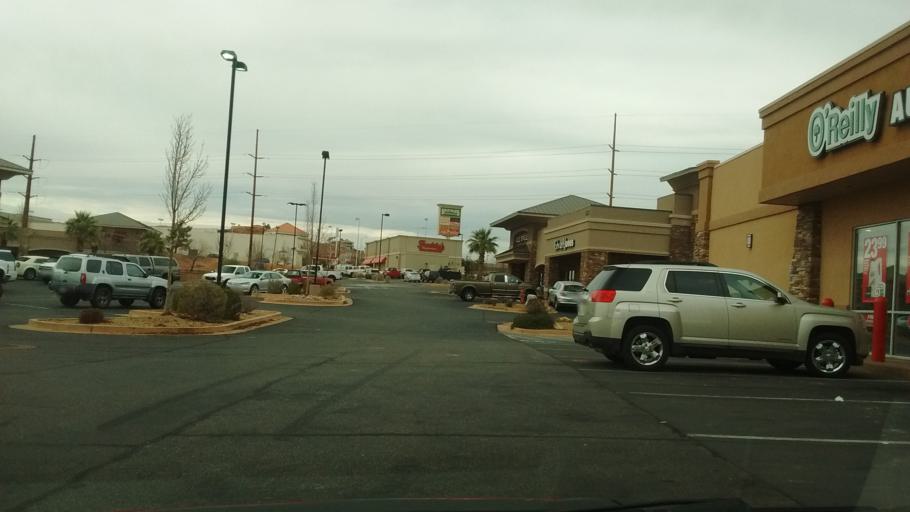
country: US
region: Utah
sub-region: Washington County
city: Washington
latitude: 37.1244
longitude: -113.5217
